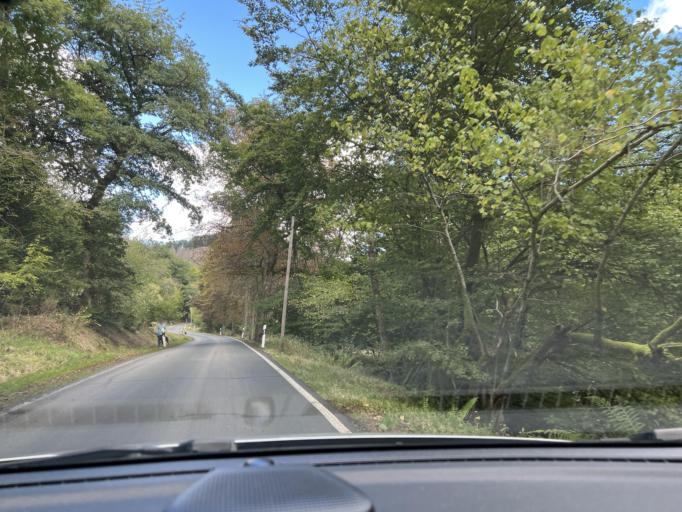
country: DE
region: North Rhine-Westphalia
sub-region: Regierungsbezirk Arnsberg
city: Bad Laasphe
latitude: 50.9569
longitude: 8.4042
